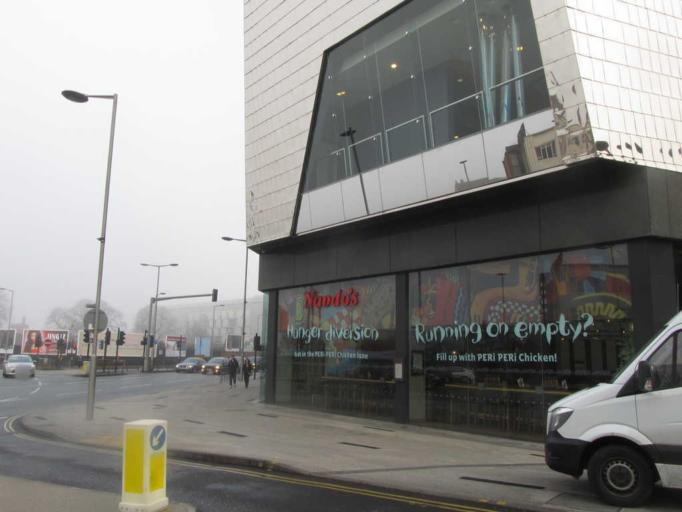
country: GB
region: England
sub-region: City of Leicester
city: Leicester
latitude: 52.6366
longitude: -1.1396
